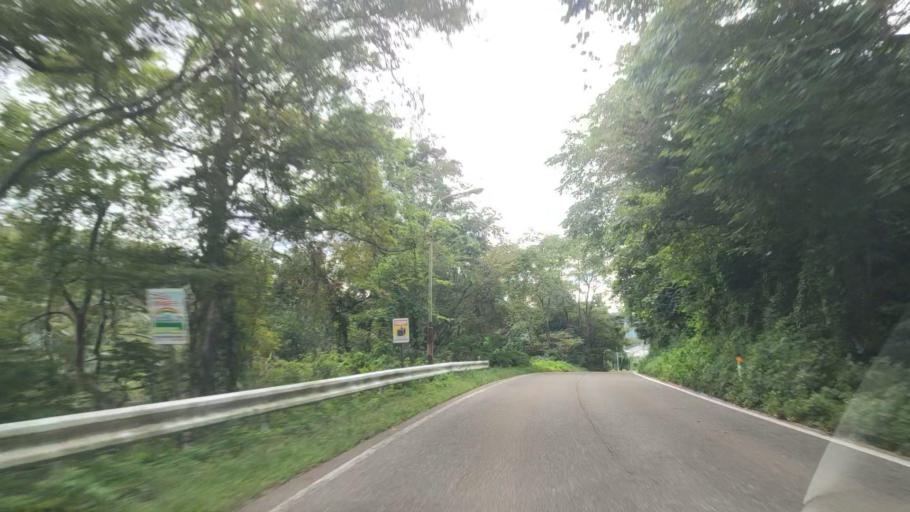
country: JP
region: Niigata
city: Arai
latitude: 36.9962
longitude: 138.2684
